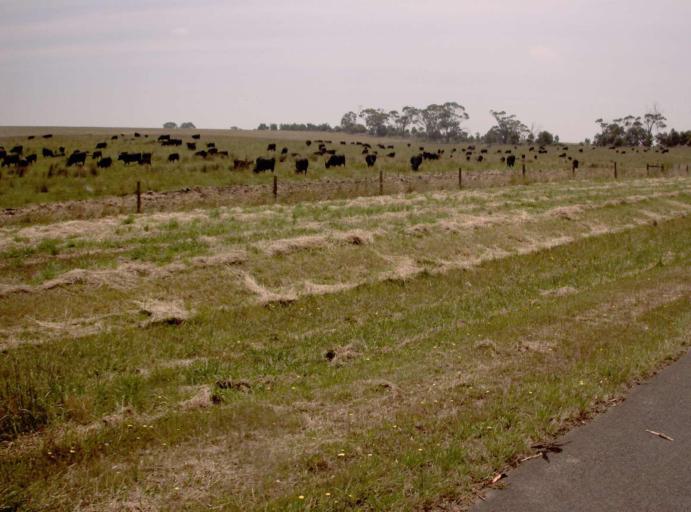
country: AU
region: Victoria
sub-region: Latrobe
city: Traralgon
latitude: -38.2532
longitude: 146.6144
